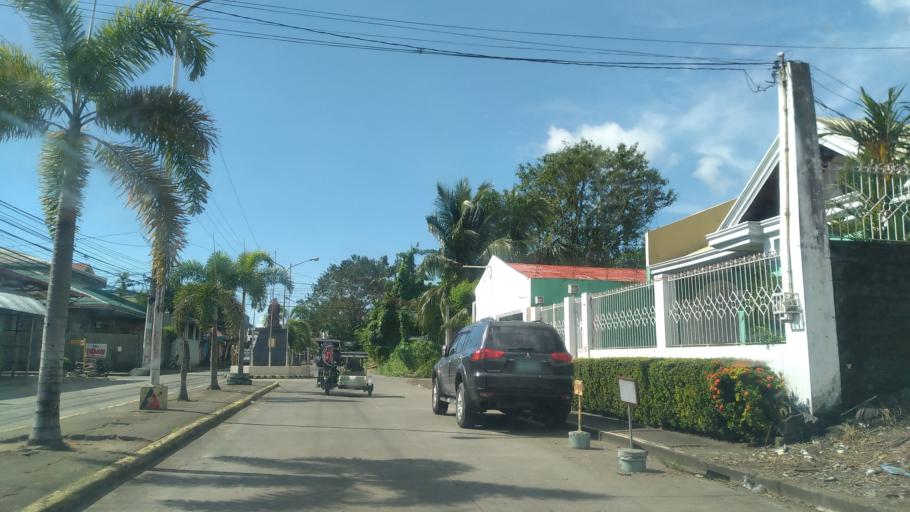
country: PH
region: Calabarzon
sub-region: Province of Quezon
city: Lucena
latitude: 13.9389
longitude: 121.6016
